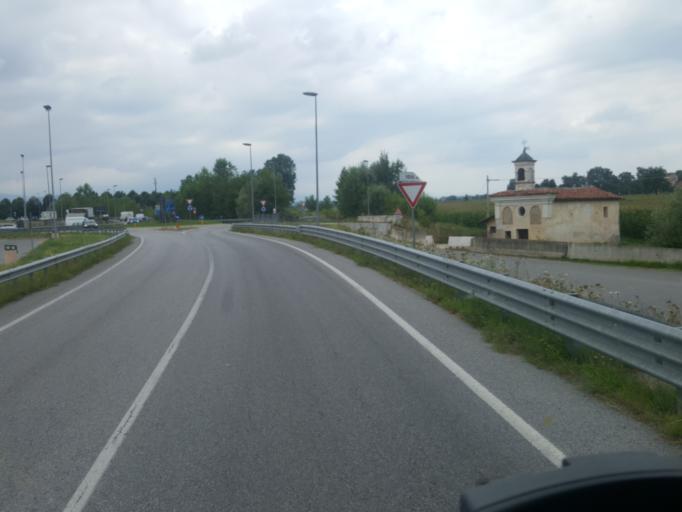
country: IT
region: Piedmont
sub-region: Provincia di Cuneo
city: Briaglia
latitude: 44.4243
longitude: 7.8520
